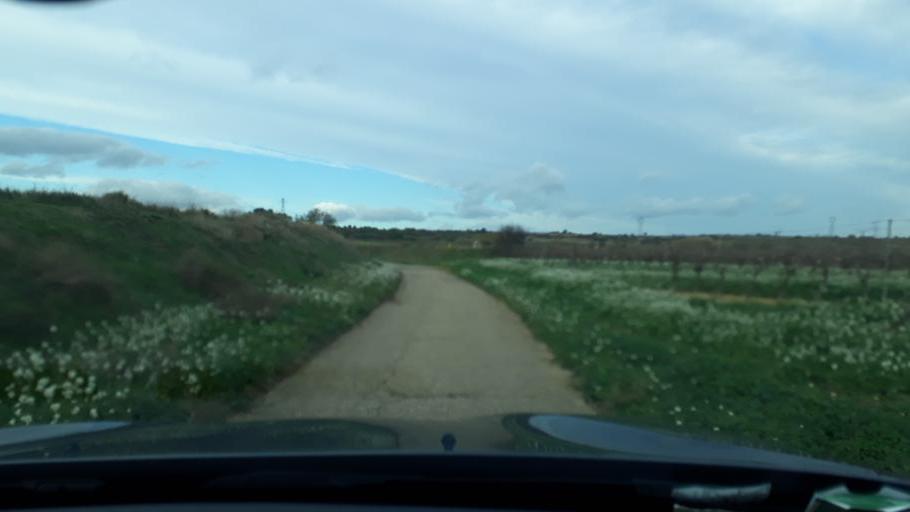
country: FR
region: Languedoc-Roussillon
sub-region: Departement de l'Herault
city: Florensac
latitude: 43.4053
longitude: 3.4601
